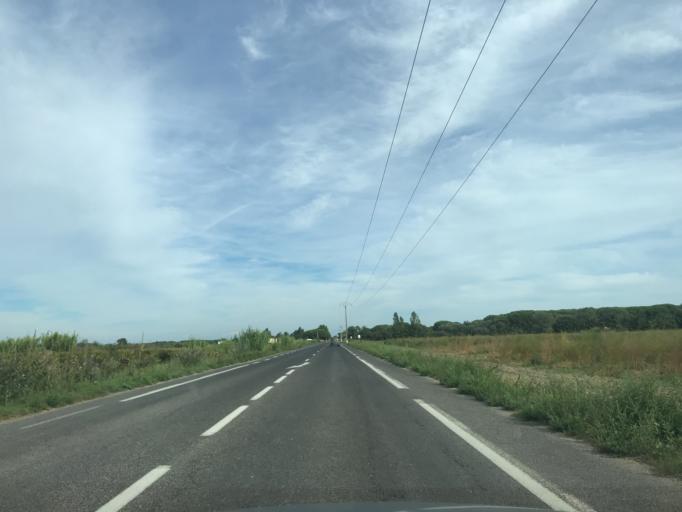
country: FR
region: Languedoc-Roussillon
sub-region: Departement du Gard
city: Aigues-Mortes
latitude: 43.5798
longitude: 4.2737
